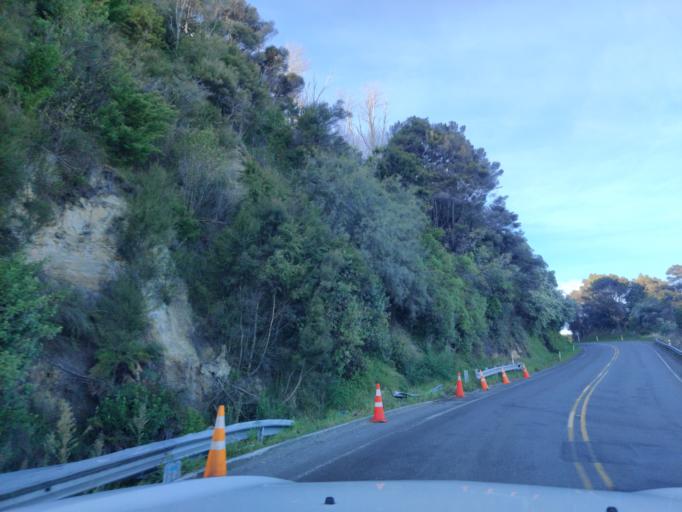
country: NZ
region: Manawatu-Wanganui
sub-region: Palmerston North City
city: Palmerston North
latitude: -40.2822
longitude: 175.7720
